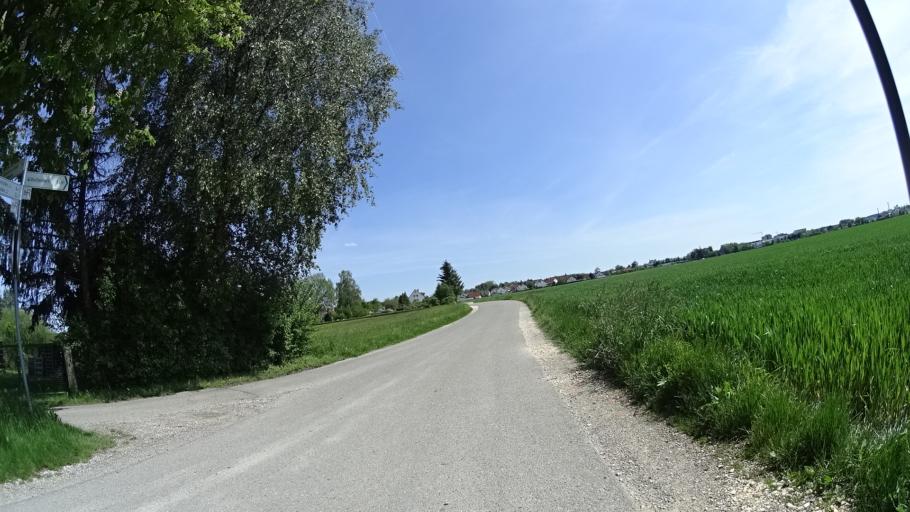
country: DE
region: Bavaria
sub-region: Swabia
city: Weissenhorn
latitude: 48.3148
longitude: 10.1499
